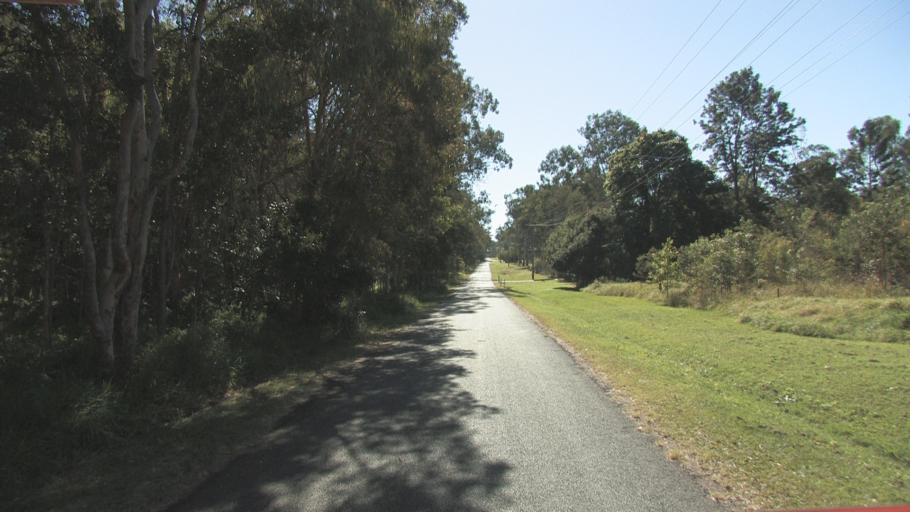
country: AU
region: Queensland
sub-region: Logan
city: Park Ridge South
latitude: -27.6966
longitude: 153.0044
